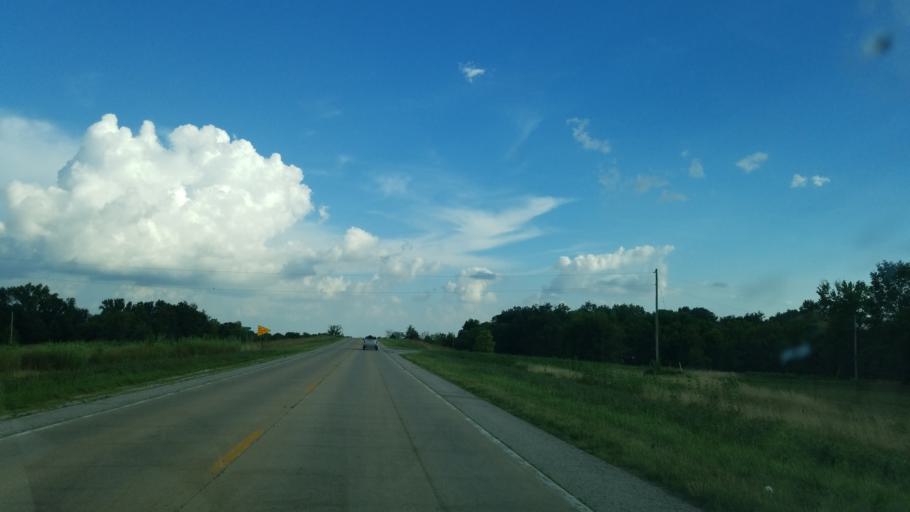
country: US
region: Illinois
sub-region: Marion County
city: Sandoval
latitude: 38.5843
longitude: -89.1084
